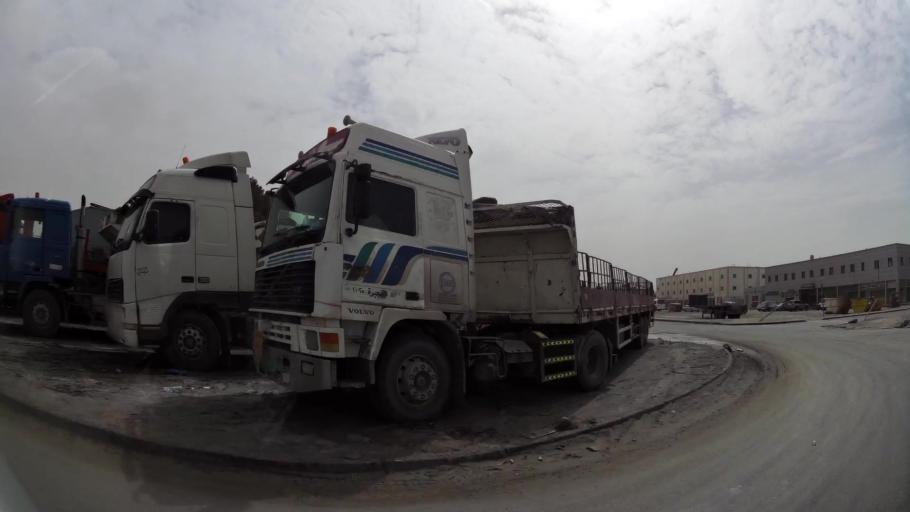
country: AE
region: Abu Dhabi
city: Abu Dhabi
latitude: 24.3532
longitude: 54.4656
